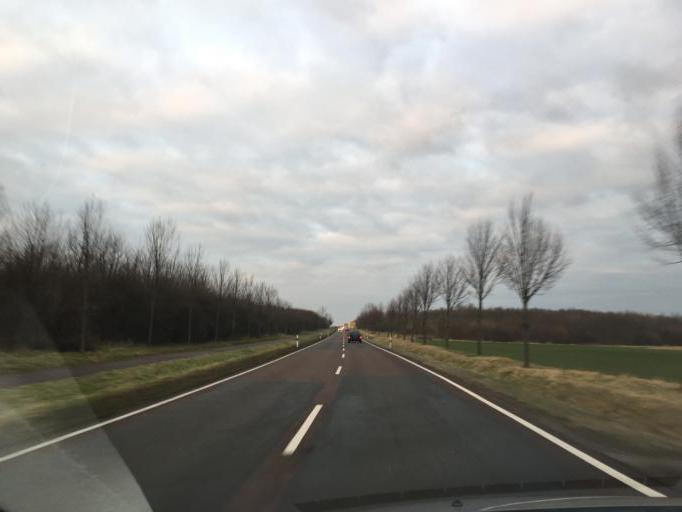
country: DE
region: Saxony
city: Grossposna
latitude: 51.2290
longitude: 12.4841
